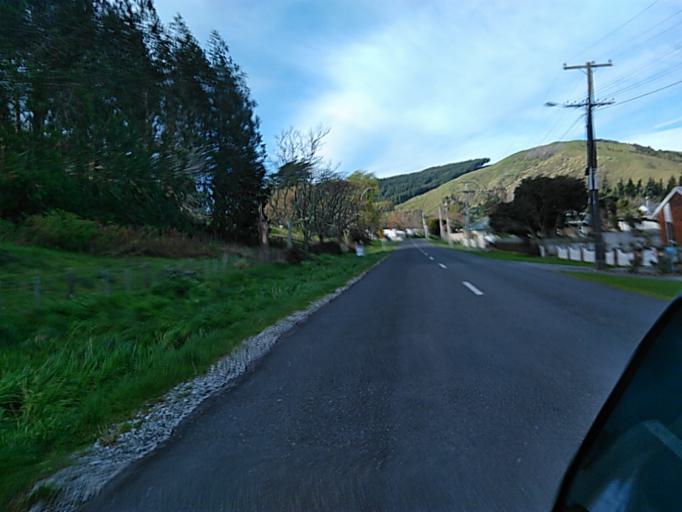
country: NZ
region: Gisborne
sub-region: Gisborne District
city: Gisborne
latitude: -38.6614
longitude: 178.0493
